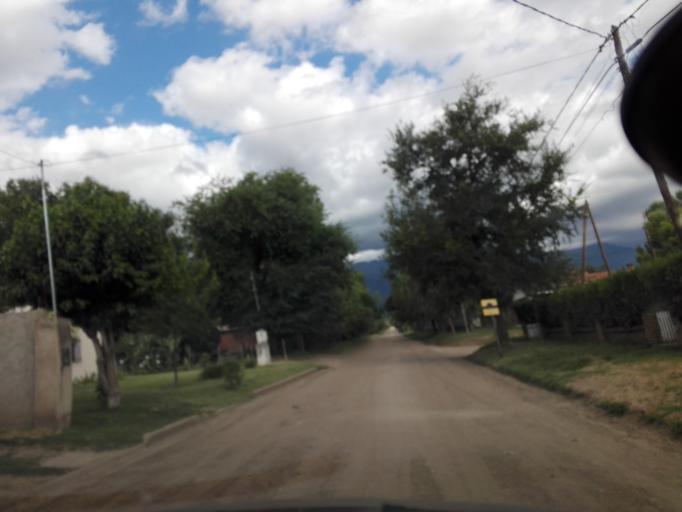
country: AR
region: Cordoba
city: Villa Las Rosas
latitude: -31.9473
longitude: -65.0494
